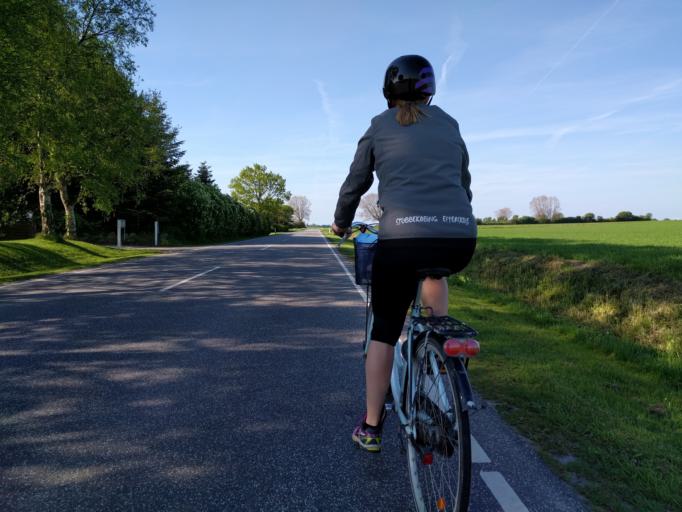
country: DK
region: Zealand
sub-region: Guldborgsund Kommune
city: Stubbekobing
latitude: 54.7911
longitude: 11.9898
